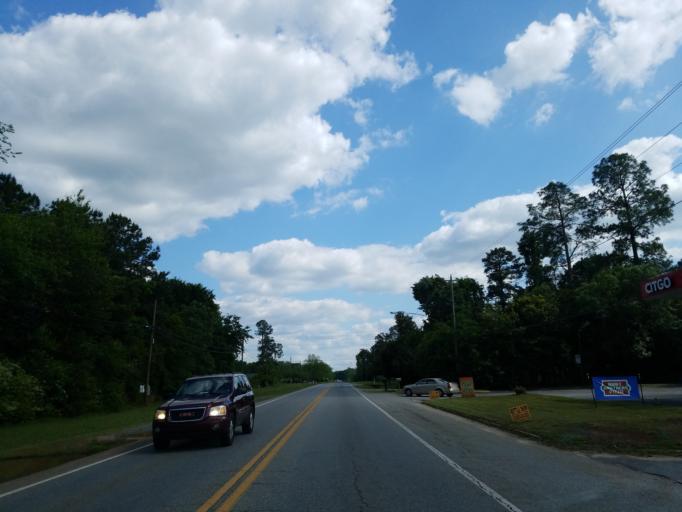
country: US
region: Georgia
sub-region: Peach County
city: Fort Valley
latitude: 32.5423
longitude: -83.8777
